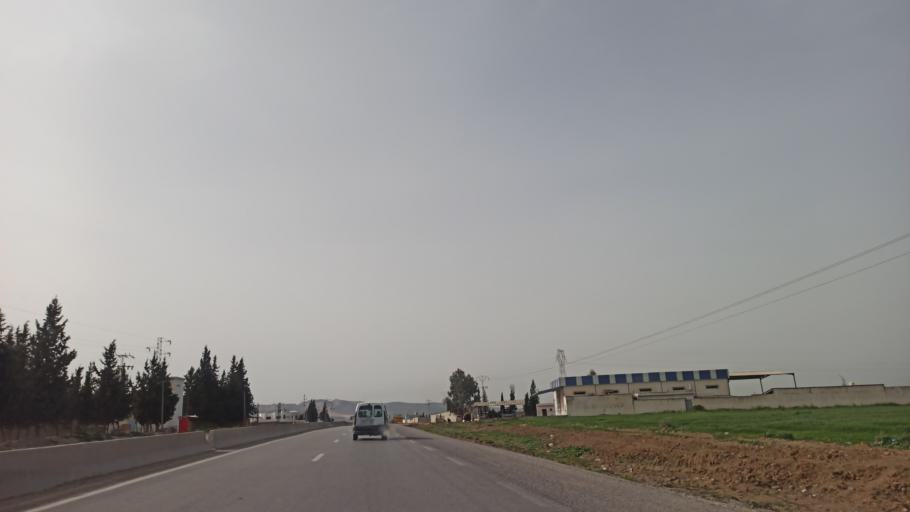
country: TN
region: Tunis
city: La Mohammedia
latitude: 36.5752
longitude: 10.0902
